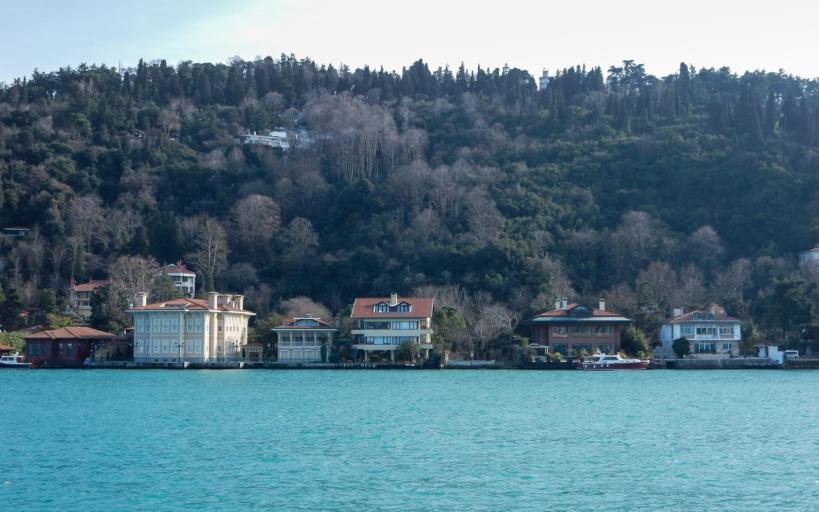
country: TR
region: Istanbul
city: UEskuedar
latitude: 41.0661
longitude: 29.0533
